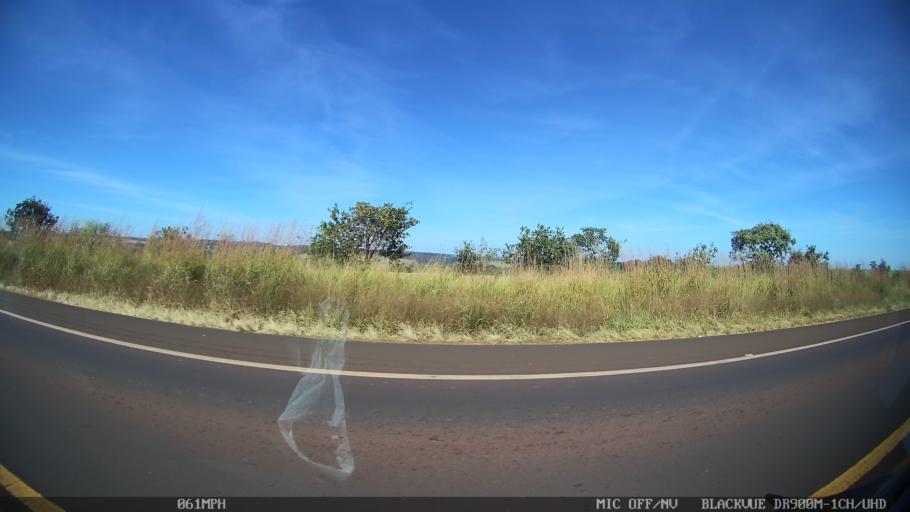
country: BR
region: Sao Paulo
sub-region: Franca
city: Franca
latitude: -20.5544
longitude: -47.4934
